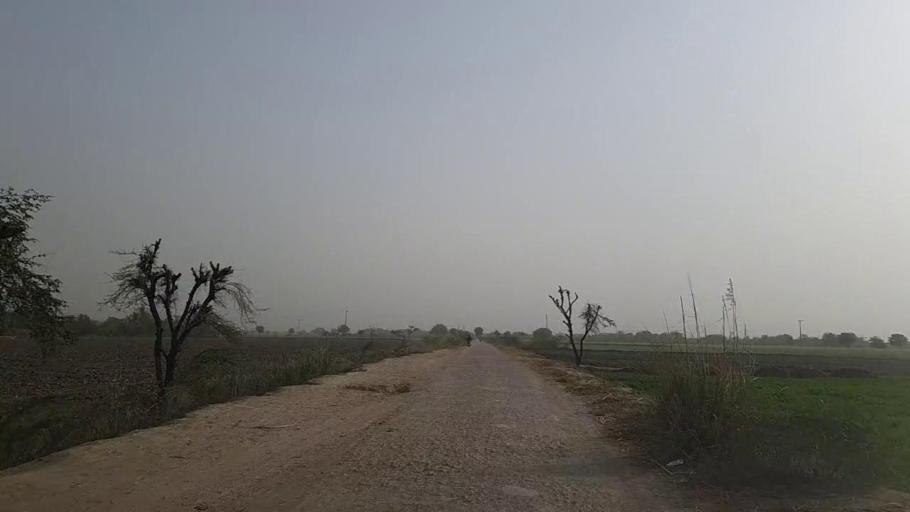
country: PK
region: Sindh
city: Pithoro
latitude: 25.4024
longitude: 69.2638
